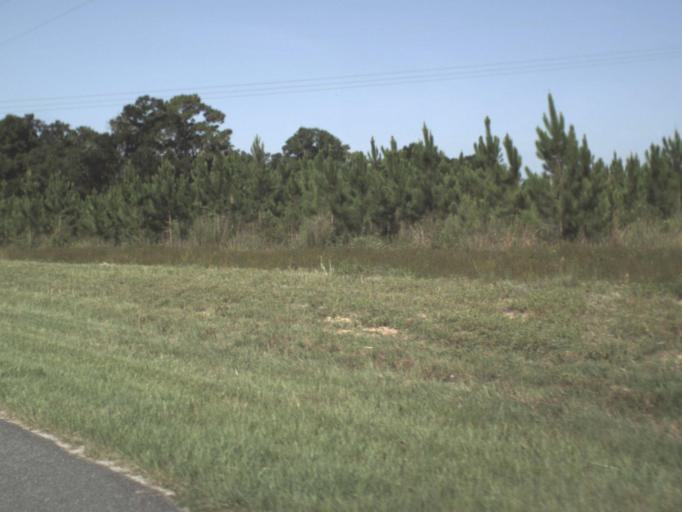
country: US
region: Florida
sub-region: Alachua County
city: High Springs
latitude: 29.8896
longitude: -82.7307
